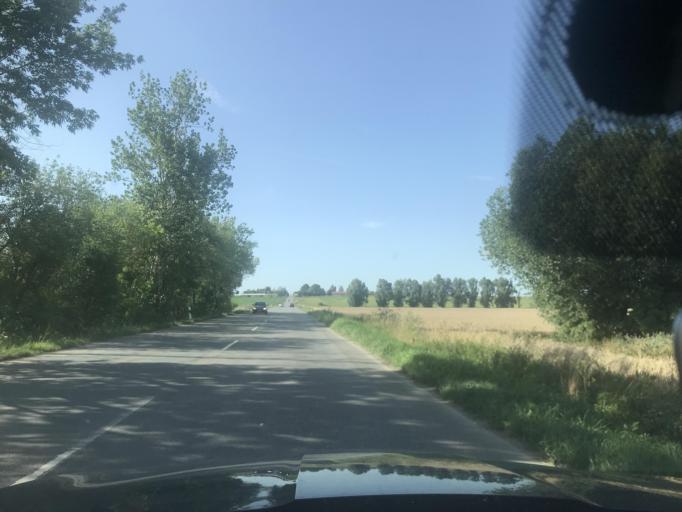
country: DE
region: Saxony-Anhalt
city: Gross Quenstedt
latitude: 51.9117
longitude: 11.1475
